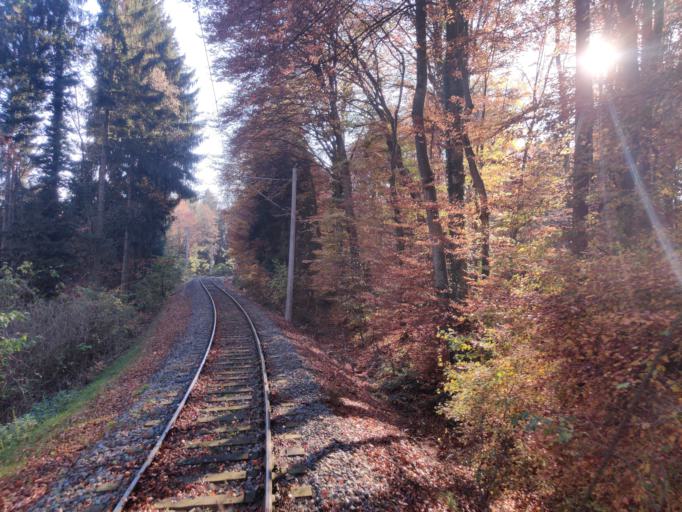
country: AT
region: Styria
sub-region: Politischer Bezirk Suedoststeiermark
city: Maierdorf
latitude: 46.8908
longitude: 15.8329
